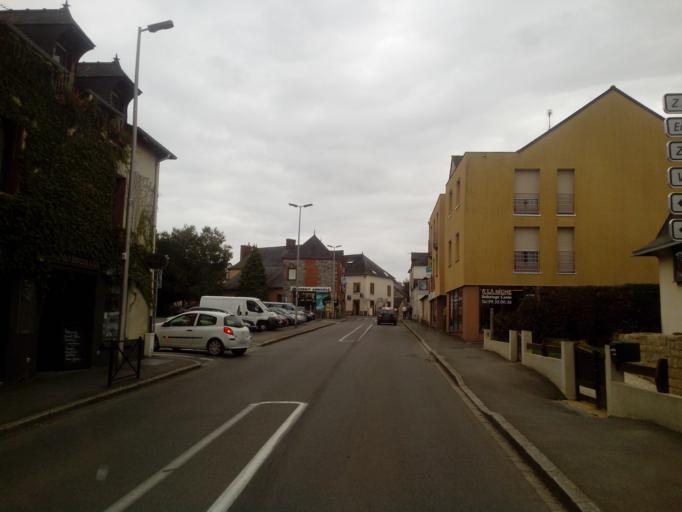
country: FR
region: Brittany
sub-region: Departement d'Ille-et-Vilaine
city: Betton
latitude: 48.1811
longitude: -1.6373
